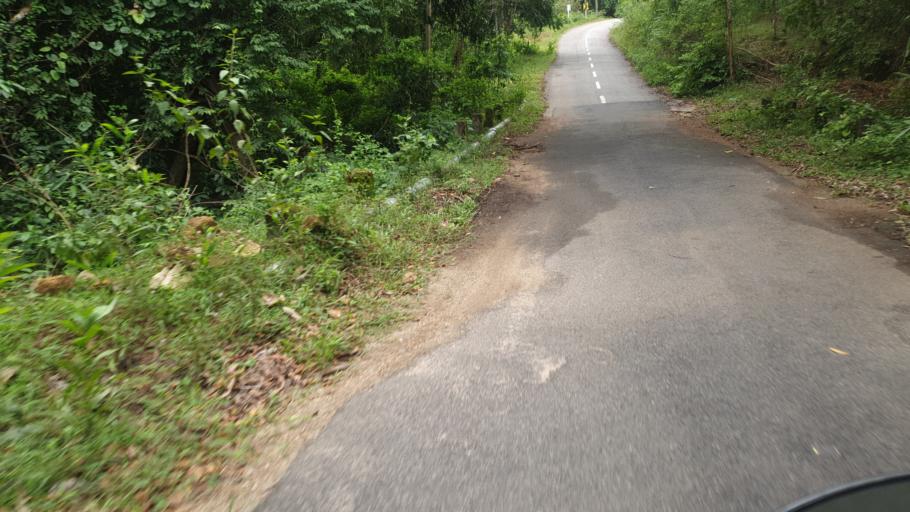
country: IN
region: Kerala
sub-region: Thiruvananthapuram
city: Nedumangad
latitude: 8.6299
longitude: 77.1263
